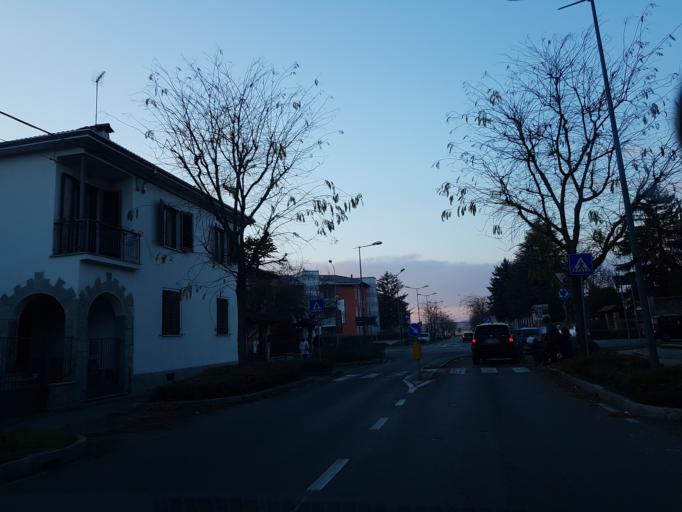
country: IT
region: Piedmont
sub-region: Provincia di Alessandria
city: Novi Ligure
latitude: 44.7645
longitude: 8.7817
